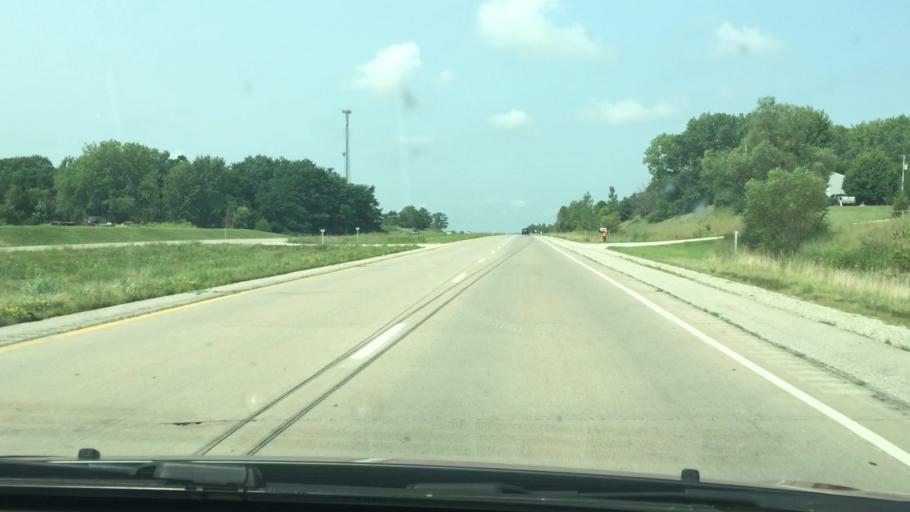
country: US
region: Iowa
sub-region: Scott County
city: Blue Grass
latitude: 41.5182
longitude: -90.8470
